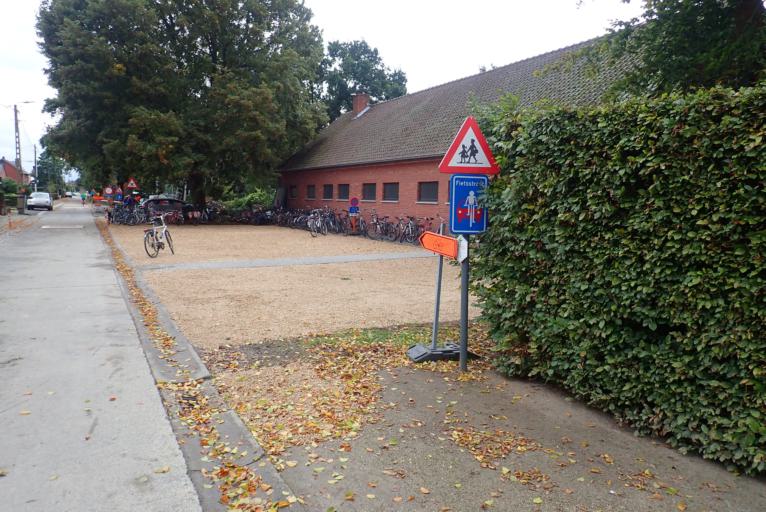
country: BE
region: Flanders
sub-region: Provincie Antwerpen
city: Berlaar
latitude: 51.0851
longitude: 4.6664
